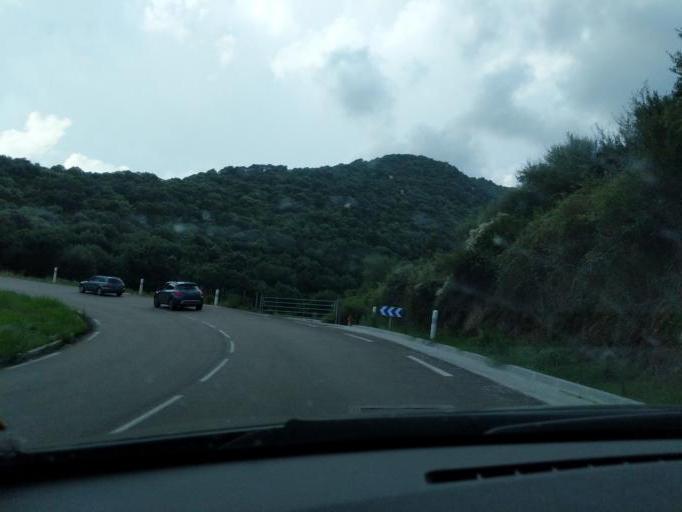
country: FR
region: Corsica
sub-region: Departement de la Corse-du-Sud
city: Sartene
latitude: 41.5800
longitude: 8.9528
